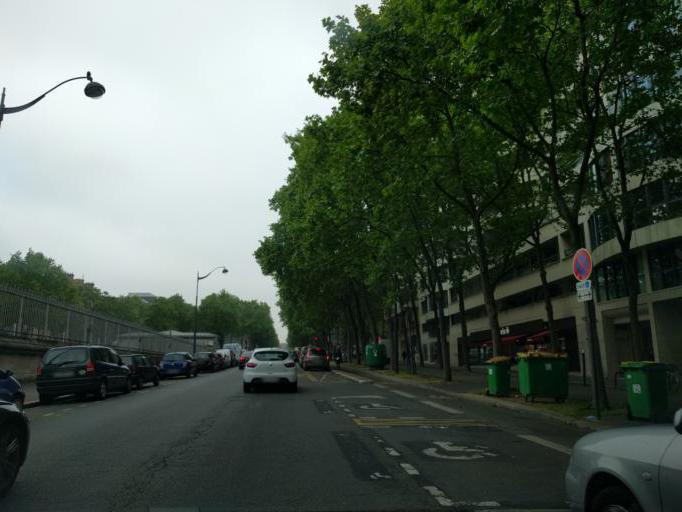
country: FR
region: Ile-de-France
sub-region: Departement du Val-de-Marne
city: Gentilly
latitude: 48.8329
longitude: 2.3377
